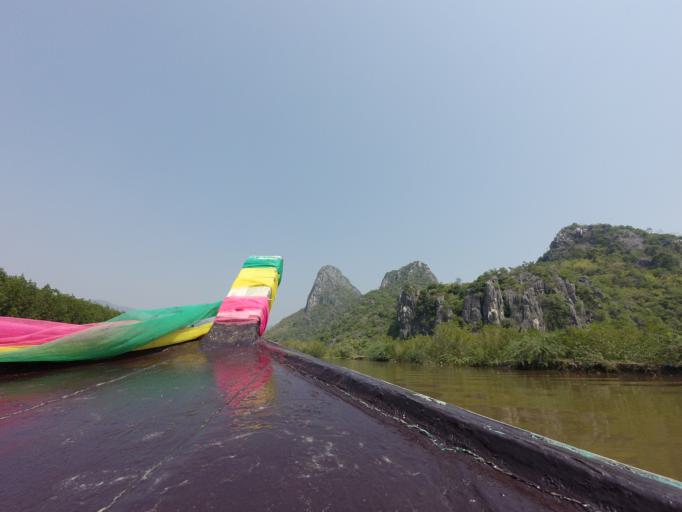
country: TH
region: Prachuap Khiri Khan
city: Kui Buri
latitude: 12.1430
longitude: 99.9525
